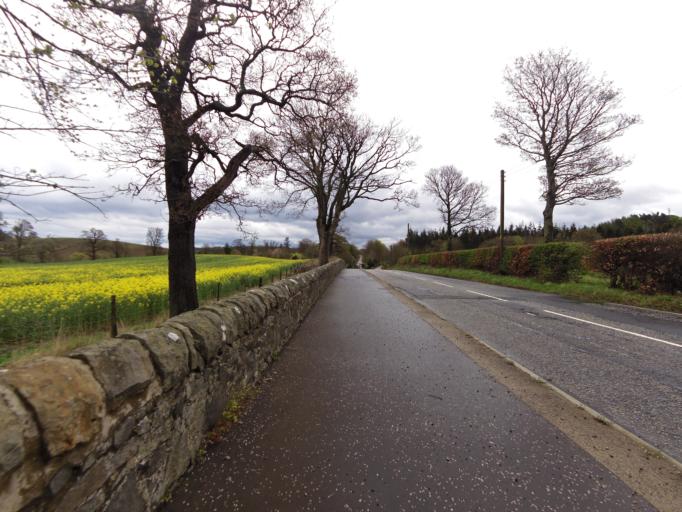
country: GB
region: Scotland
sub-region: Edinburgh
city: Queensferry
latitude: 55.9814
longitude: -3.3504
